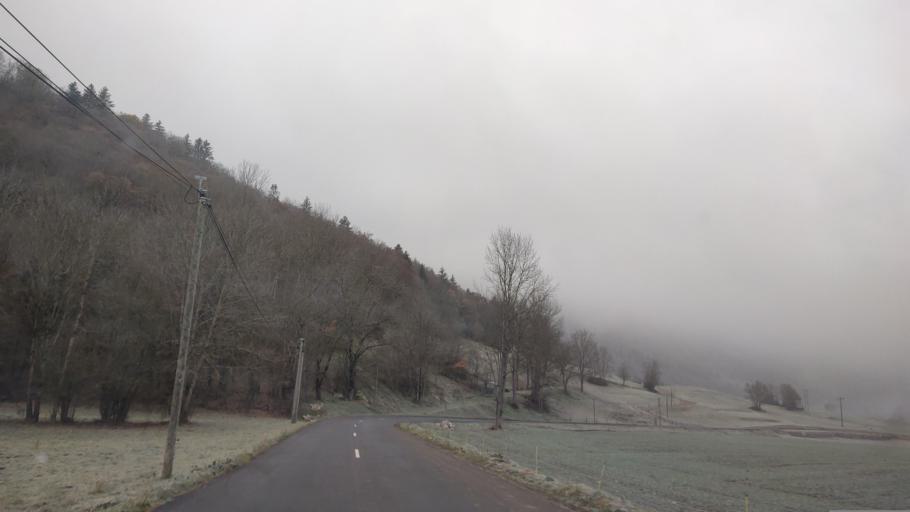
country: FR
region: Rhone-Alpes
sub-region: Departement de la Savoie
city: Coise-Saint-Jean-Pied-Gauthier
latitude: 45.6049
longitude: 6.1411
